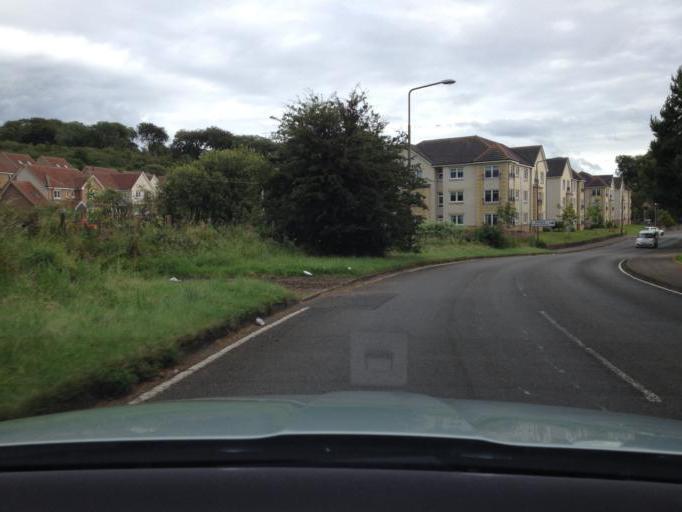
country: GB
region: Scotland
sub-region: West Lothian
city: Bathgate
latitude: 55.9111
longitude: -3.6379
